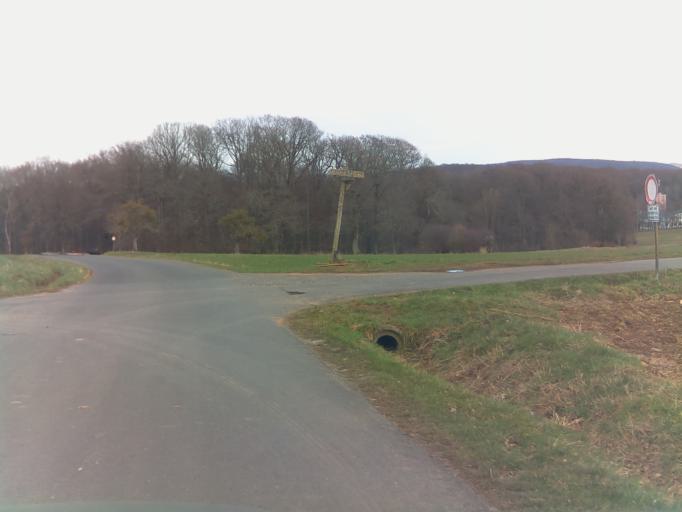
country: DE
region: Rheinland-Pfalz
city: Kirschweiler
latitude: 49.7500
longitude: 7.2334
